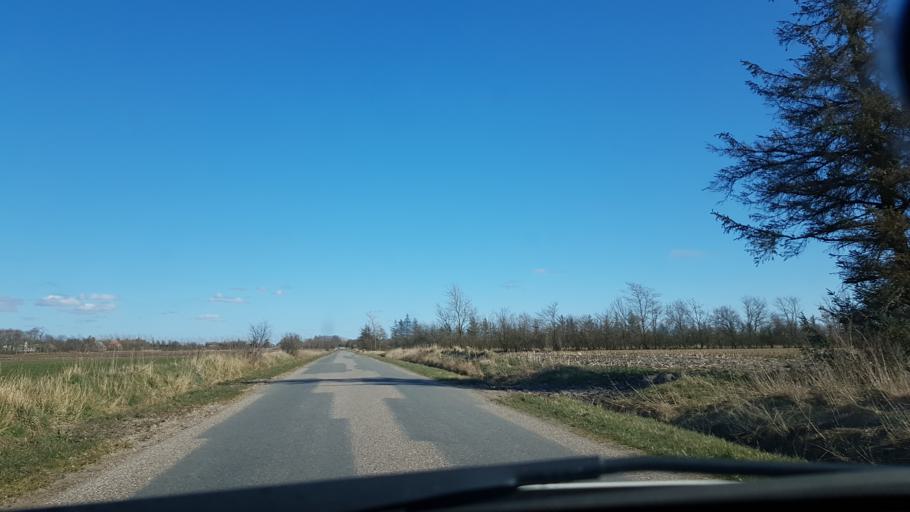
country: DK
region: South Denmark
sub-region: Tonder Kommune
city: Sherrebek
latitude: 55.2290
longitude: 8.7460
